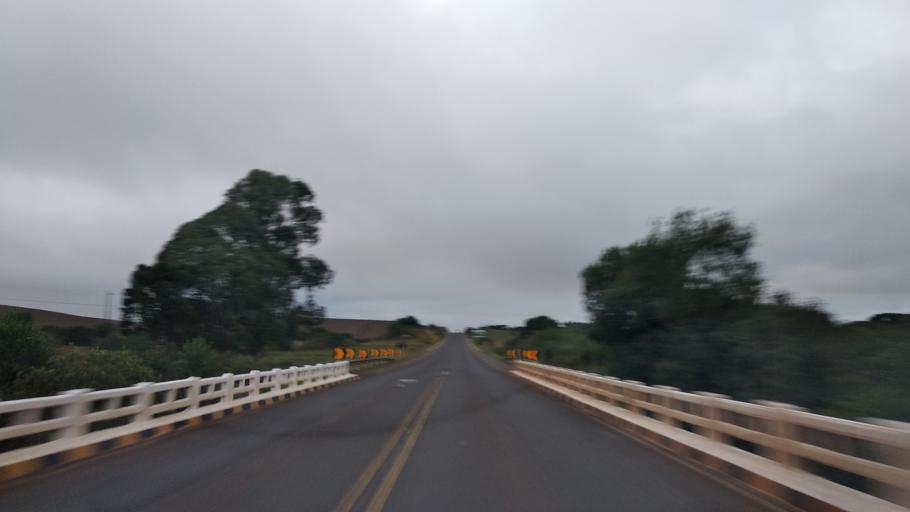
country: BR
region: Santa Catarina
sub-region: Campos Novos
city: Campos Novos
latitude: -27.3793
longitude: -51.0626
